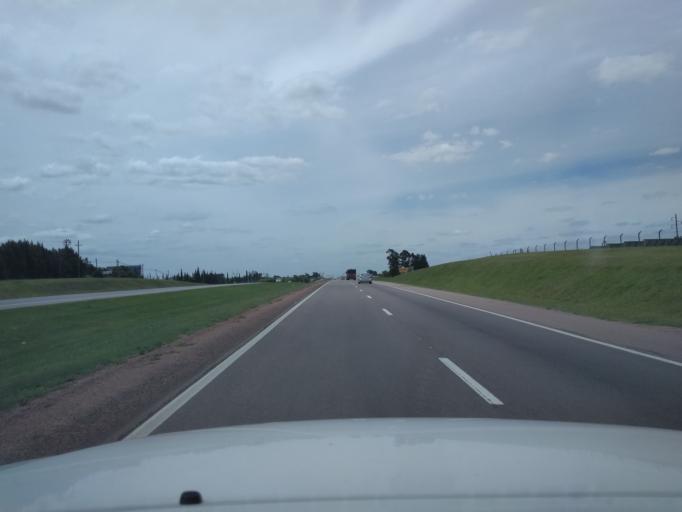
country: UY
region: Canelones
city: Las Piedras
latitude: -34.7339
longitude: -56.2494
